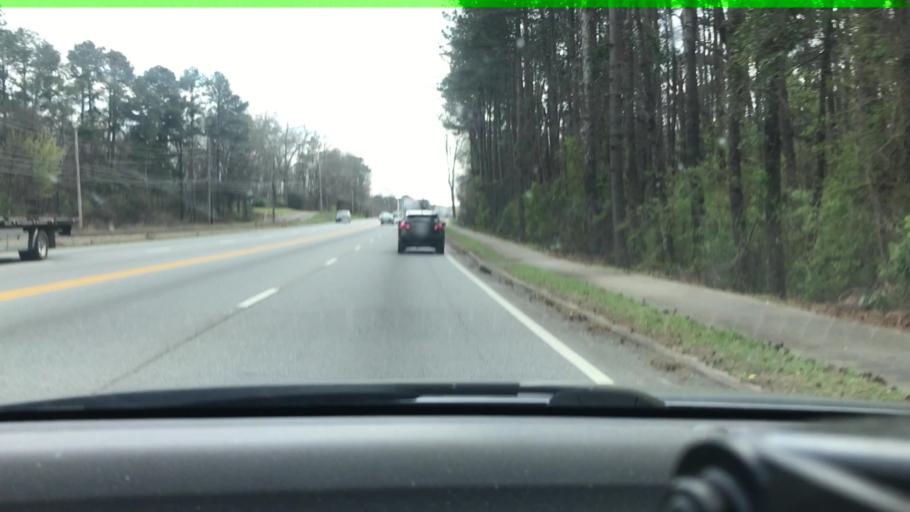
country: US
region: Georgia
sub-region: Clarke County
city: Country Club Estates
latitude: 33.9812
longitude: -83.4161
